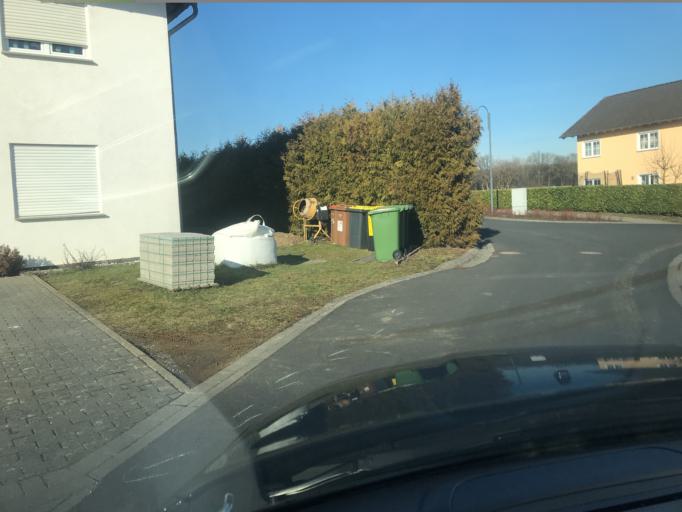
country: DE
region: Rheinland-Pfalz
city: Gorgeshausen
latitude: 50.4222
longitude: 7.9438
